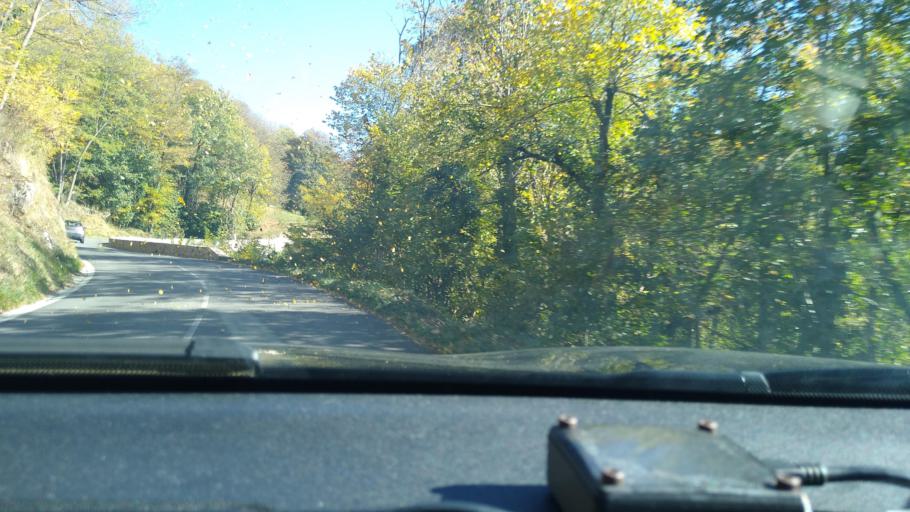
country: FR
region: Midi-Pyrenees
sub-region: Departement de l'Ariege
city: Ax-les-Thermes
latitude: 42.7227
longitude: 1.8421
